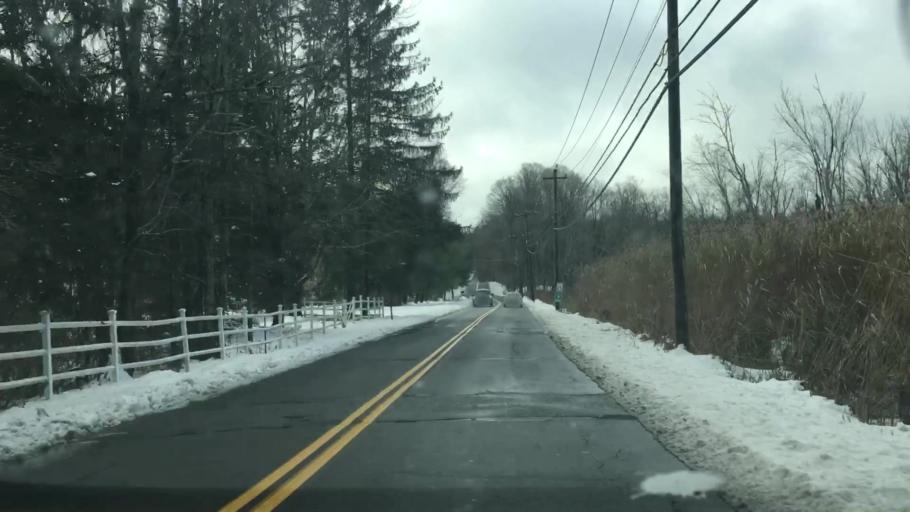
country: US
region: Connecticut
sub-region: Fairfield County
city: Danbury
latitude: 41.3636
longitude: -73.5041
